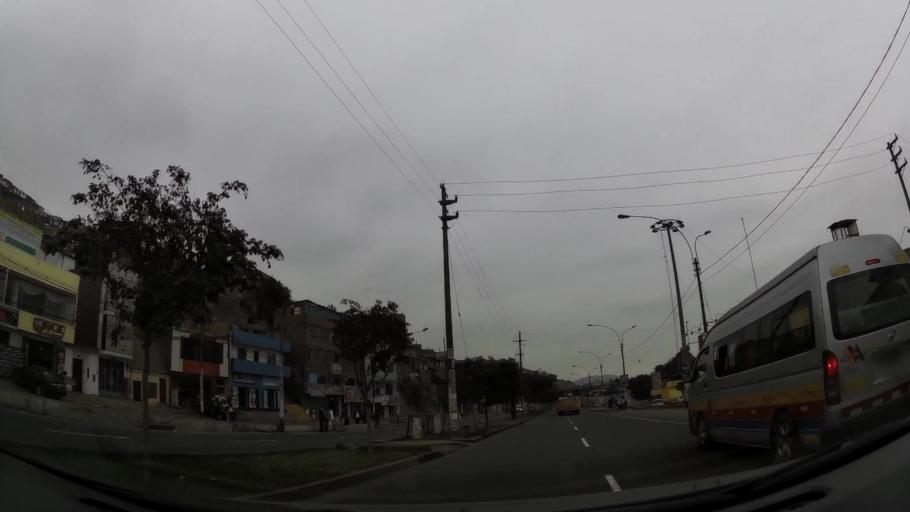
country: PE
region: Lima
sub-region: Lima
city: Independencia
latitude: -11.9620
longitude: -77.0546
